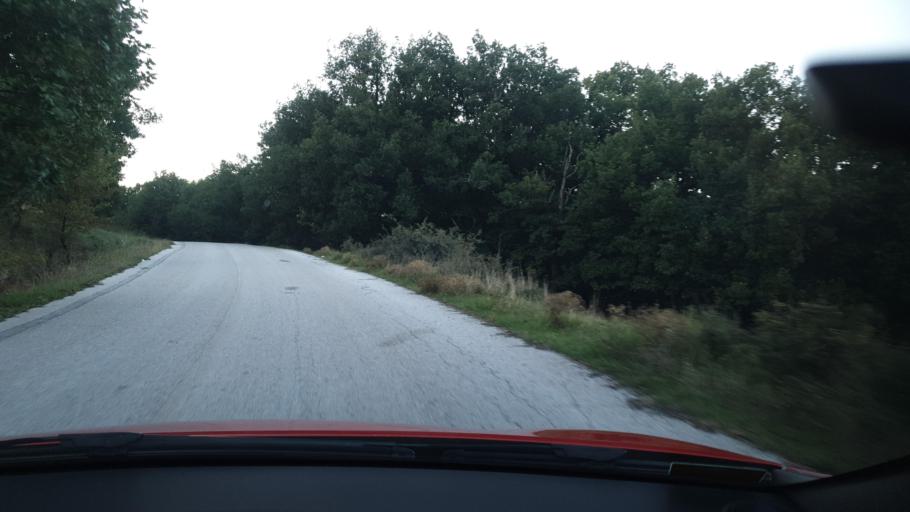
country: GR
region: Central Macedonia
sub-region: Nomos Thessalonikis
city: Peristera
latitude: 40.5151
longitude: 23.2143
